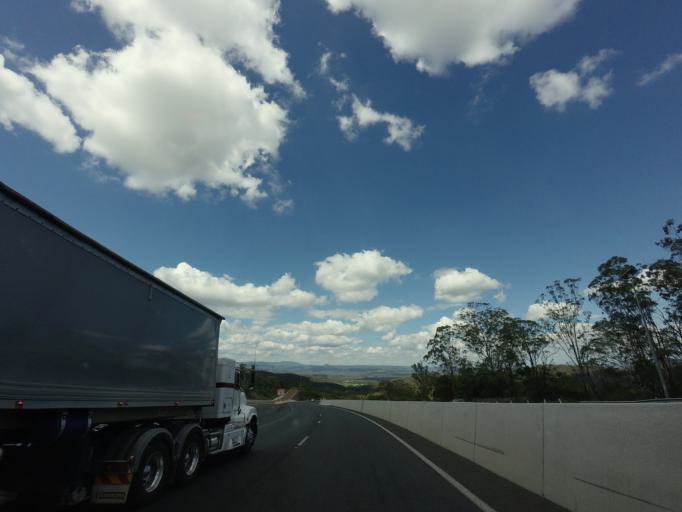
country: AU
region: Queensland
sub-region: Toowoomba
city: East Toowoomba
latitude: -27.5707
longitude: 151.9880
